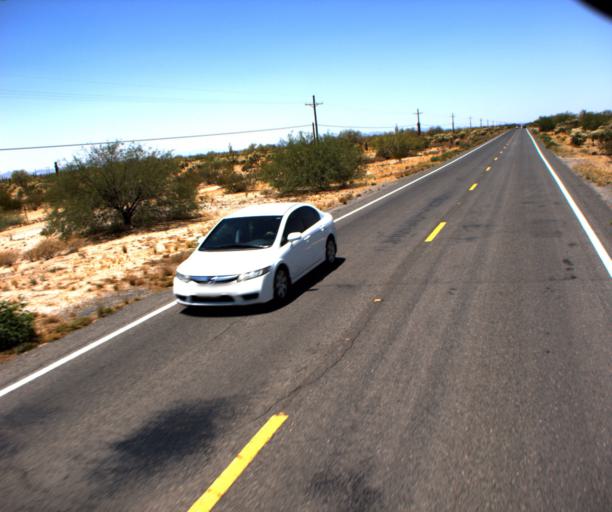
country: US
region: Arizona
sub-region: Pinal County
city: Florence
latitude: 32.9357
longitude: -111.3118
